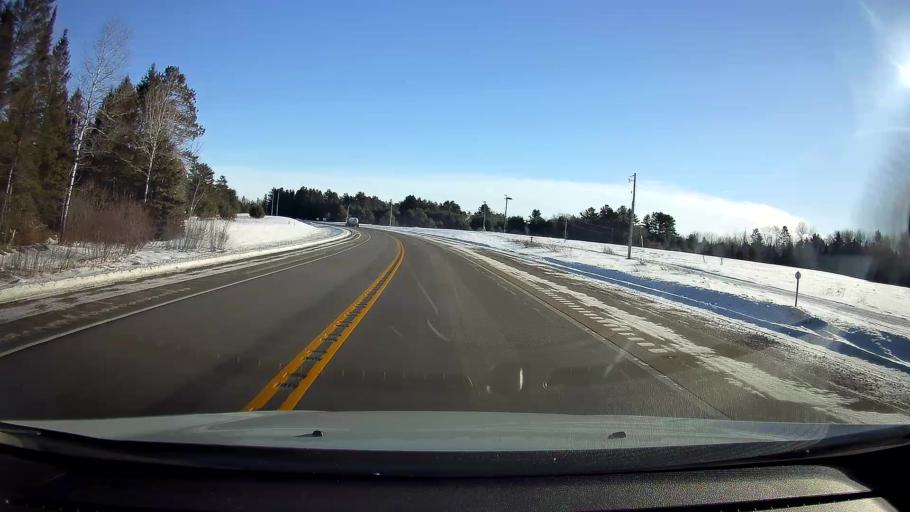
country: US
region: Wisconsin
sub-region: Sawyer County
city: Hayward
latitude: 46.0742
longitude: -91.4144
